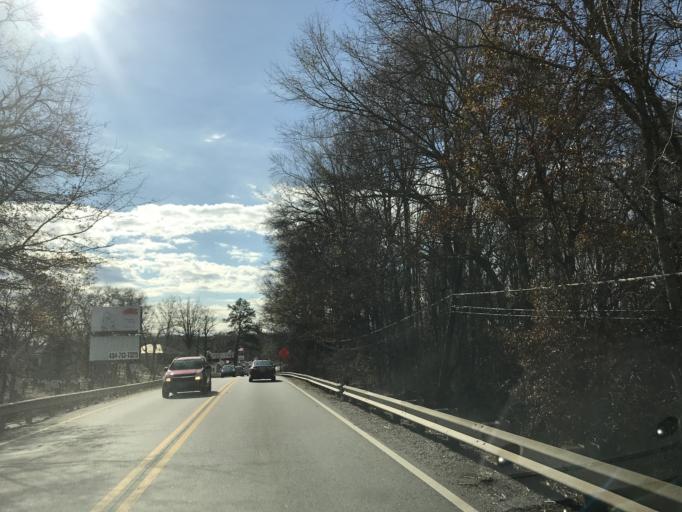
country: US
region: Georgia
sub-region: Paulding County
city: Hiram
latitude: 33.8751
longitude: -84.7626
